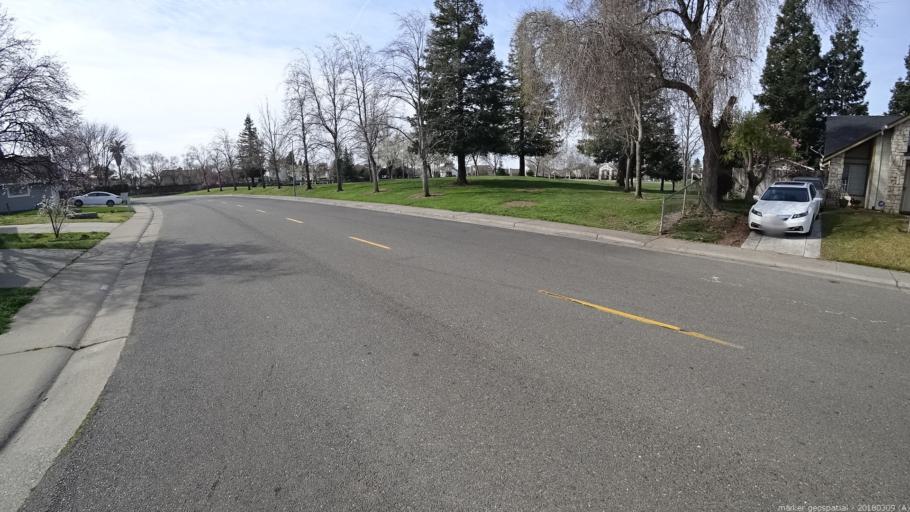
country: US
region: California
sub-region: Sacramento County
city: Florin
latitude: 38.4586
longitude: -121.4022
